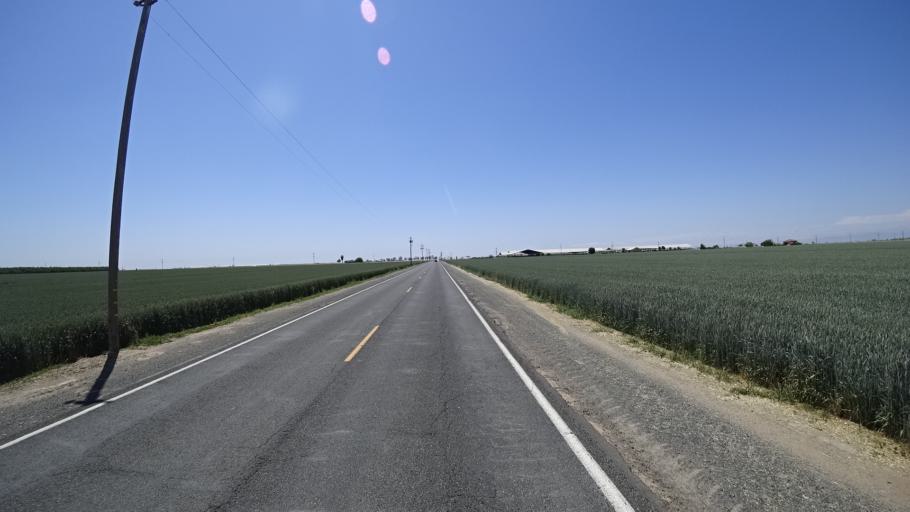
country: US
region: California
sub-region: Kings County
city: Armona
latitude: 36.2296
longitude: -119.7088
